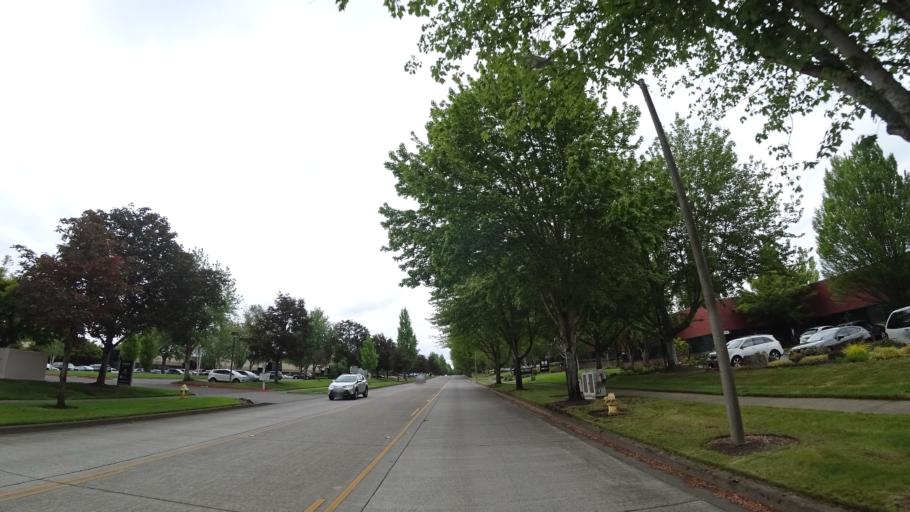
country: US
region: Oregon
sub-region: Washington County
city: Tigard
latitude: 45.4511
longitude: -122.7889
